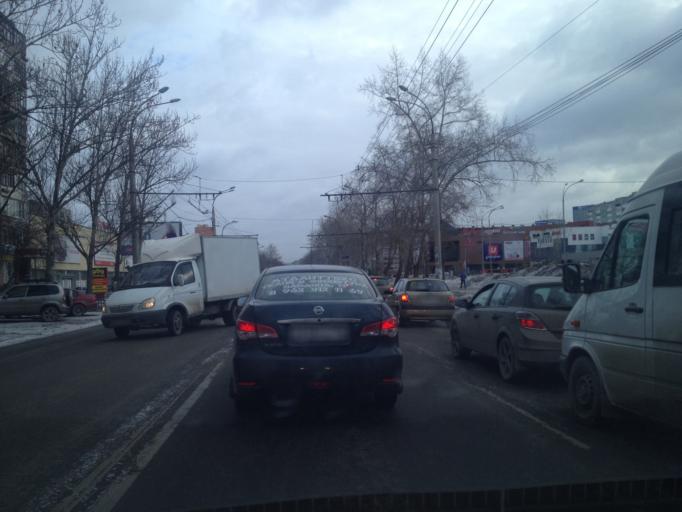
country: RU
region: Sverdlovsk
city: Sovkhoznyy
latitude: 56.7955
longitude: 60.5780
